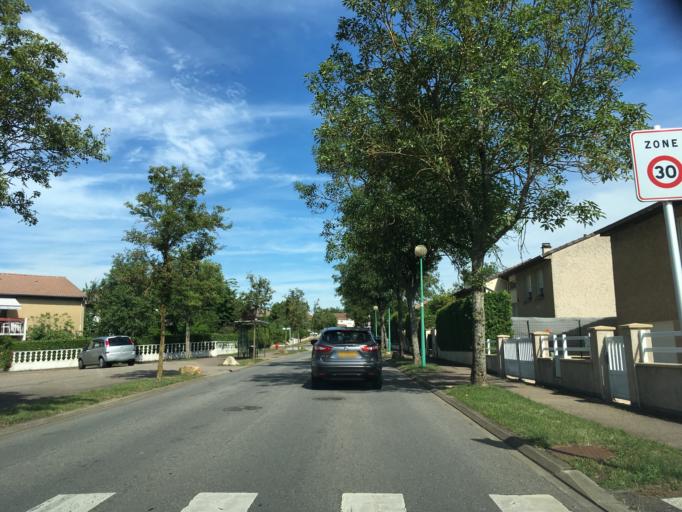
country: FR
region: Lorraine
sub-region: Departement de la Moselle
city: Fleury
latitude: 49.0713
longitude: 6.1851
